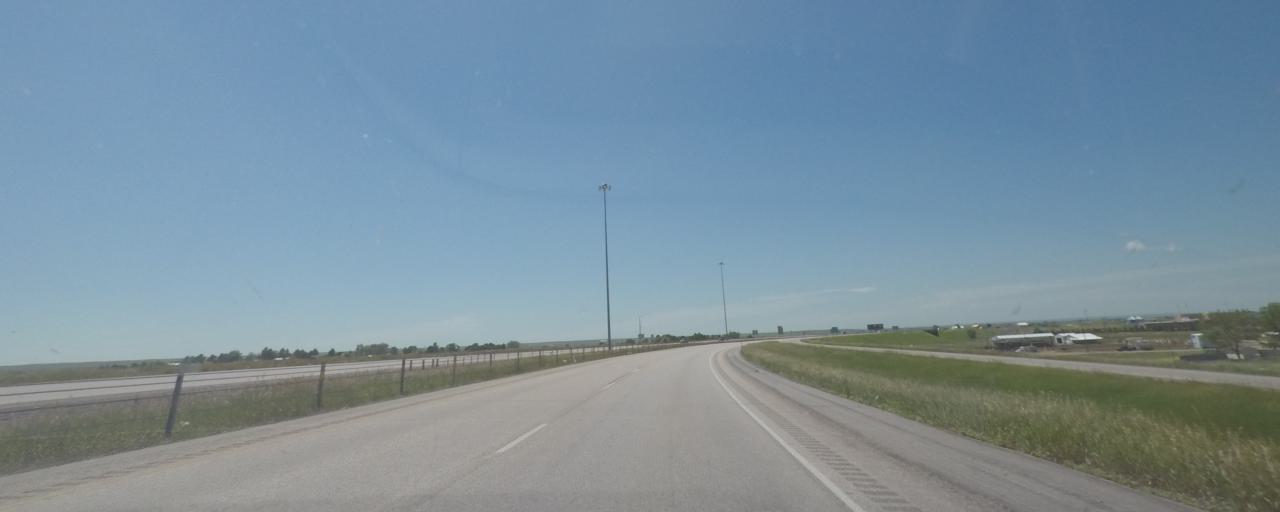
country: US
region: South Dakota
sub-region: Haakon County
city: Philip
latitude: 43.9865
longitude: -102.2406
